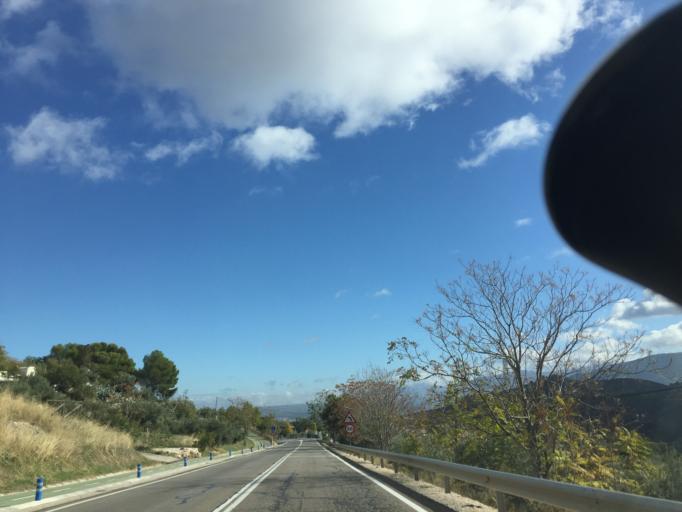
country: ES
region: Andalusia
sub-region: Provincia de Jaen
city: Jaen
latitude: 37.7519
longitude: -3.7995
